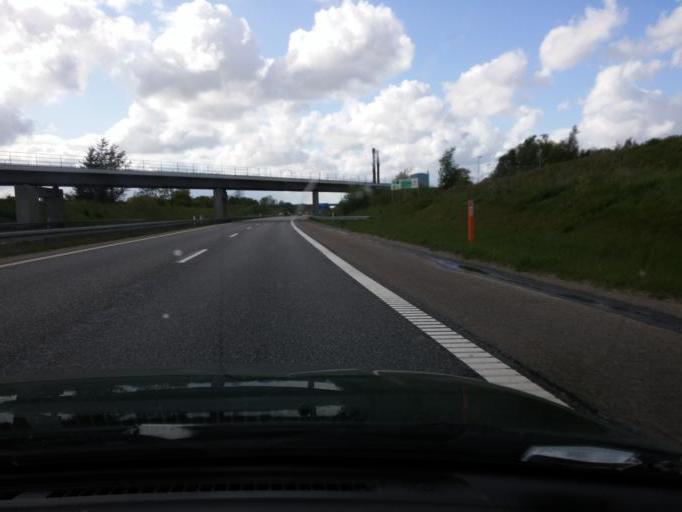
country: DK
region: South Denmark
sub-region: Faaborg-Midtfyn Kommune
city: Ringe
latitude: 55.2456
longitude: 10.4820
